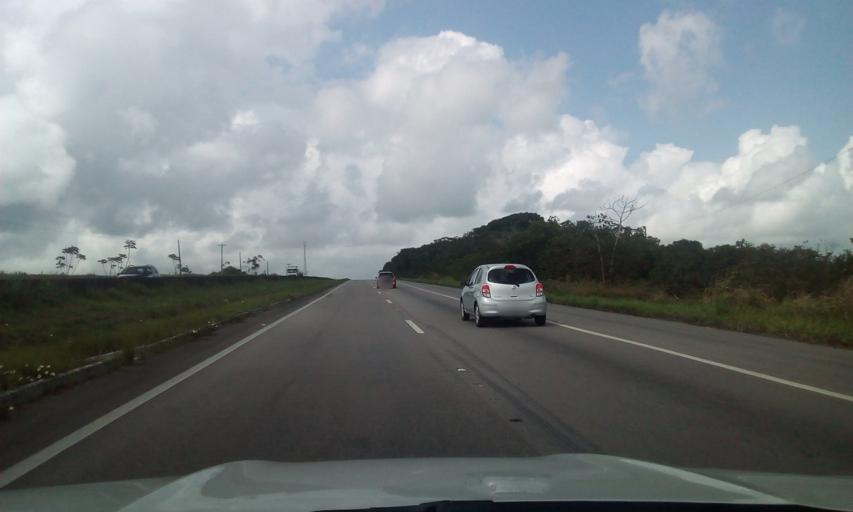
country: BR
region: Paraiba
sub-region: Alhandra
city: Alhandra
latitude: -7.4430
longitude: -34.9782
